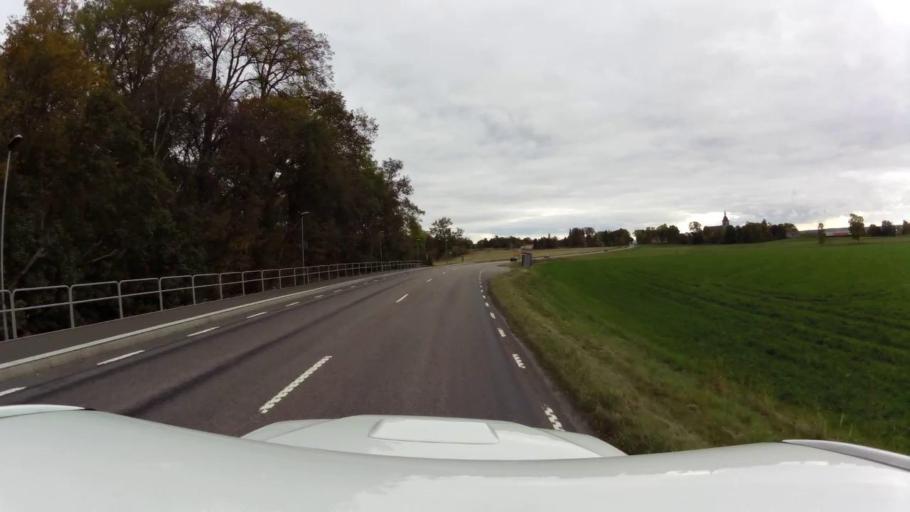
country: SE
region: OEstergoetland
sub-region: Linkopings Kommun
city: Berg
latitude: 58.4871
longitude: 15.5126
